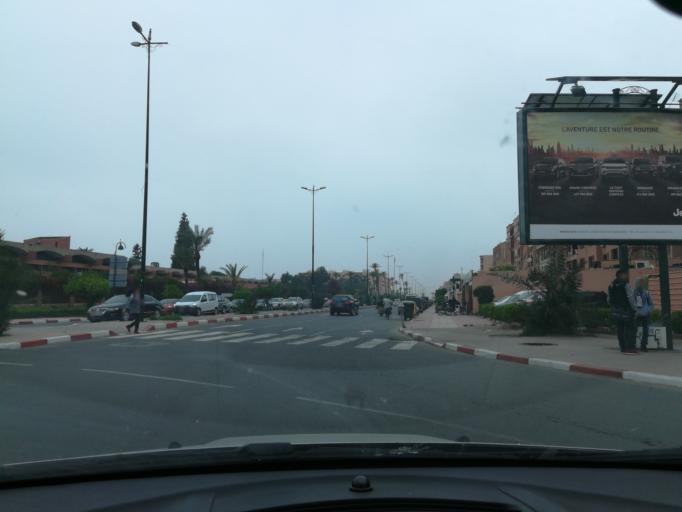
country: MA
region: Marrakech-Tensift-Al Haouz
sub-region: Marrakech
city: Marrakesh
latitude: 31.6490
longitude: -8.0136
